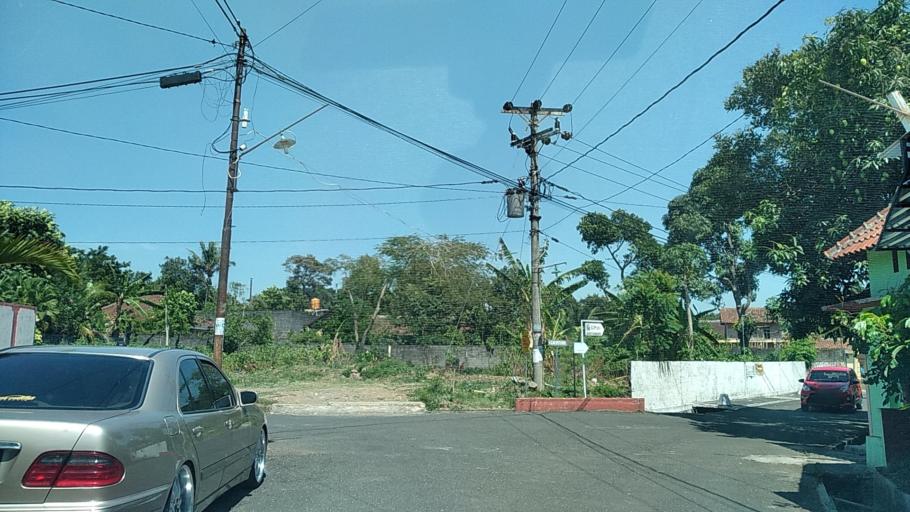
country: ID
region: Central Java
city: Ungaran
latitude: -7.0981
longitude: 110.4083
